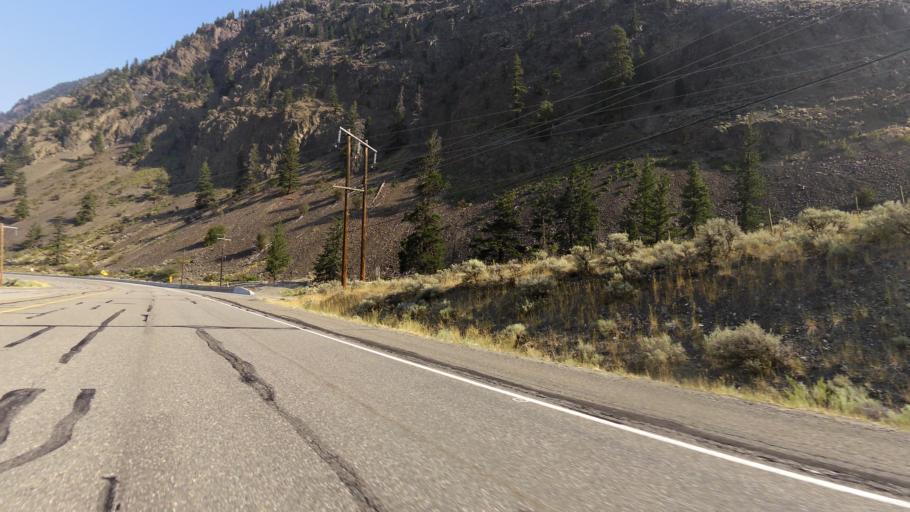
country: CA
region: British Columbia
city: Oliver
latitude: 49.2233
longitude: -119.9581
